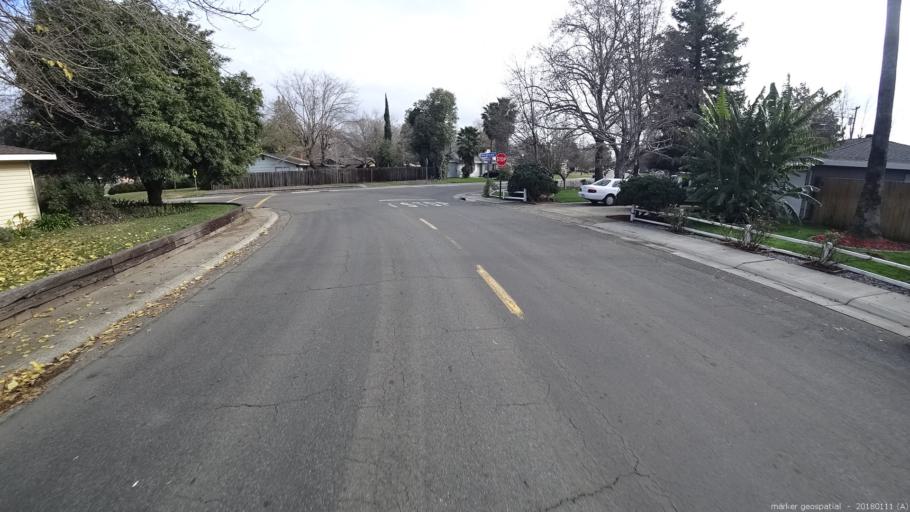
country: US
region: California
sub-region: Sacramento County
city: Rancho Cordova
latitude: 38.6056
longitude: -121.3027
